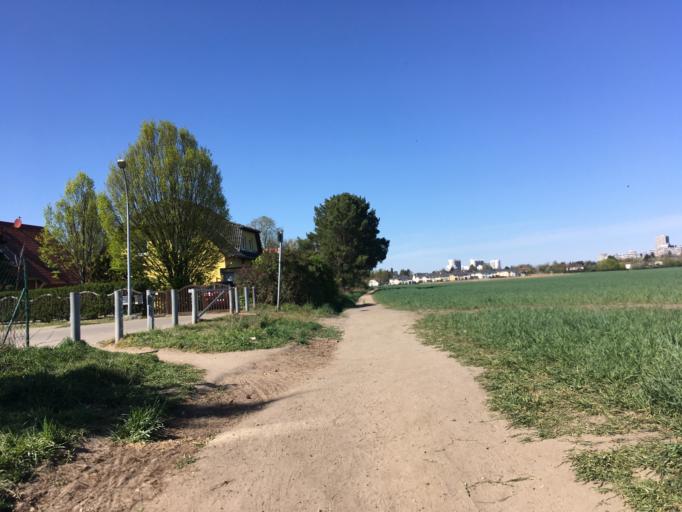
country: DE
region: Berlin
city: Gropiusstadt
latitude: 52.4134
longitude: 13.4554
